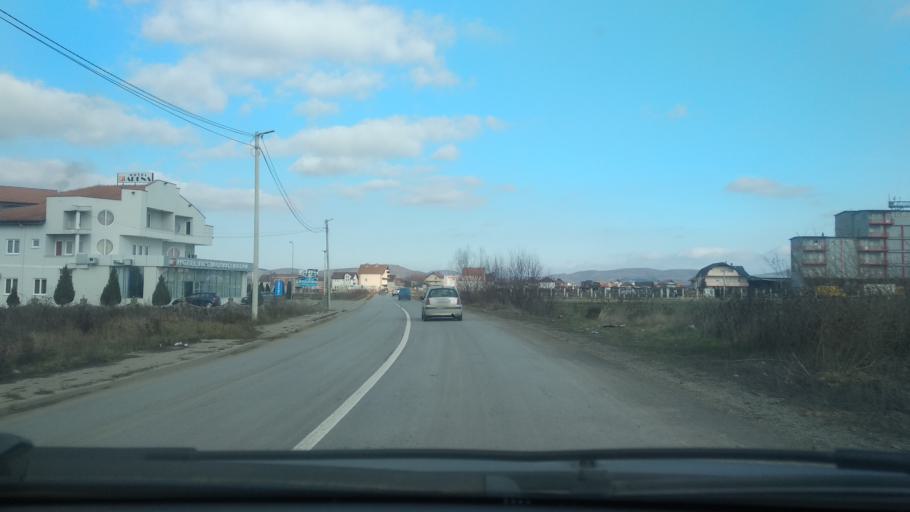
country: XK
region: Pristina
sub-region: Komuna e Obiliqit
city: Obiliq
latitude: 42.7296
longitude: 21.1021
